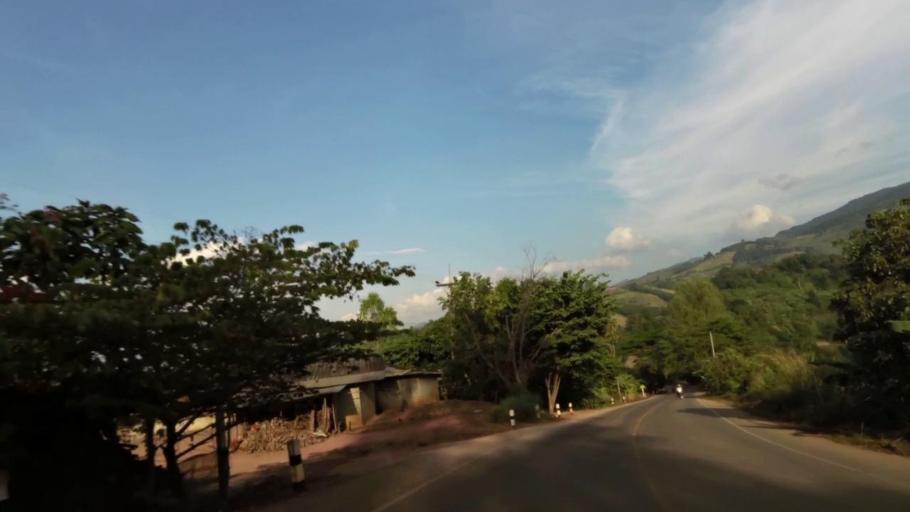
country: TH
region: Chiang Rai
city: Khun Tan
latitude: 19.8617
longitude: 100.3963
